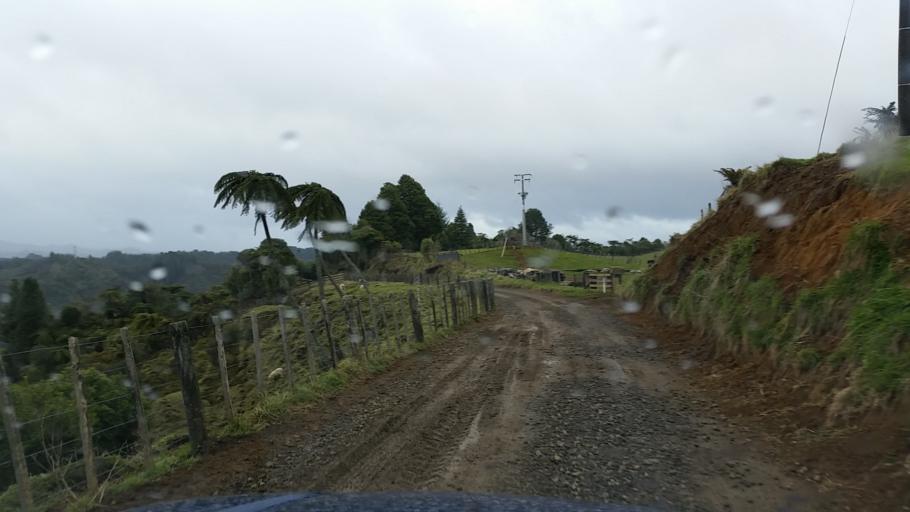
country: NZ
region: Taranaki
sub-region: South Taranaki District
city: Eltham
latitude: -39.1663
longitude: 174.6279
